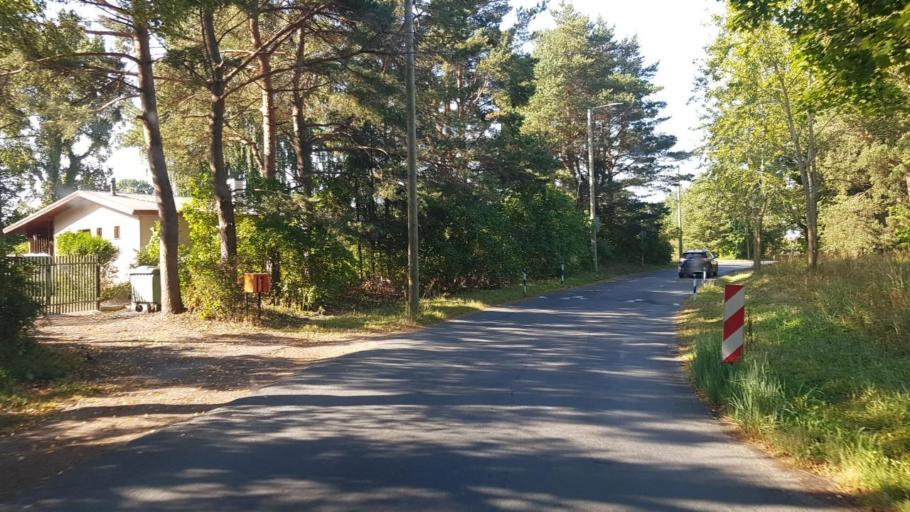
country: EE
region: Harju
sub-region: Harku vald
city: Tabasalu
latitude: 59.4347
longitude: 24.5981
